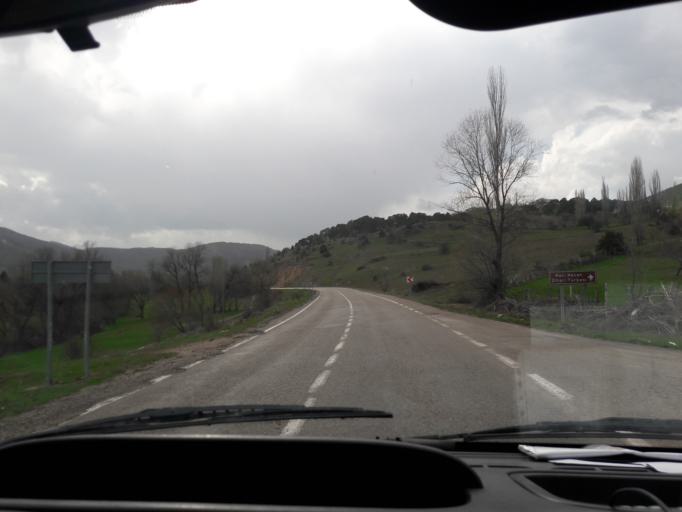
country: TR
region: Giresun
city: Alucra
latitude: 40.2648
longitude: 38.9084
